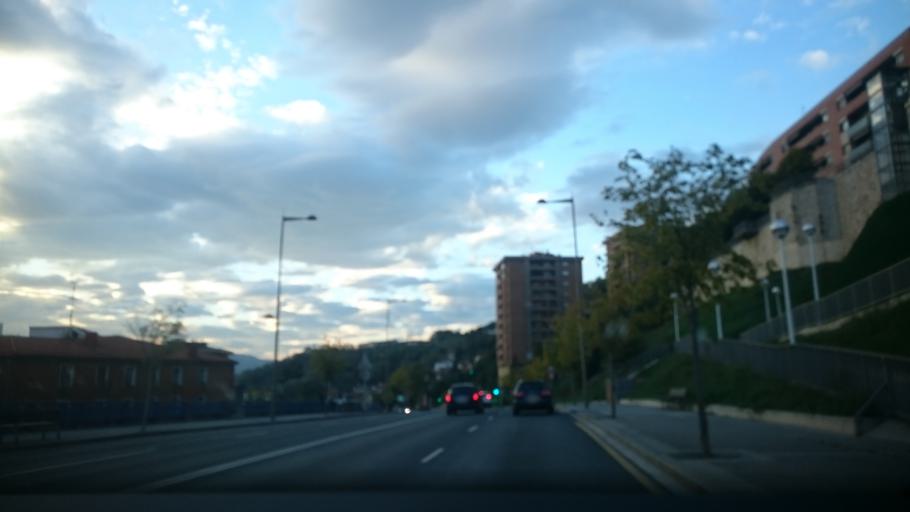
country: ES
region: Basque Country
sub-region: Bizkaia
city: Bilbao
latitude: 43.2691
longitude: -2.9208
